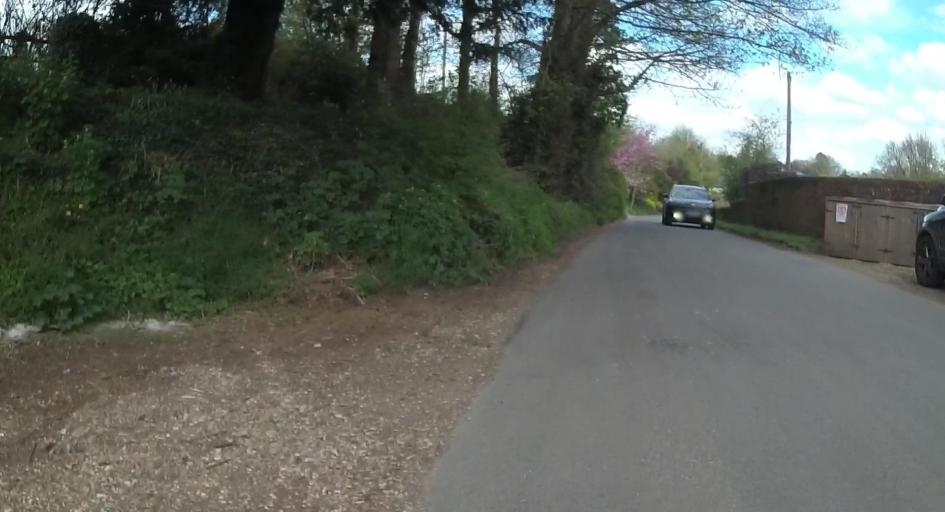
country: GB
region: England
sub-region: Hampshire
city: Abbotts Ann
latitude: 51.1285
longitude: -1.4925
